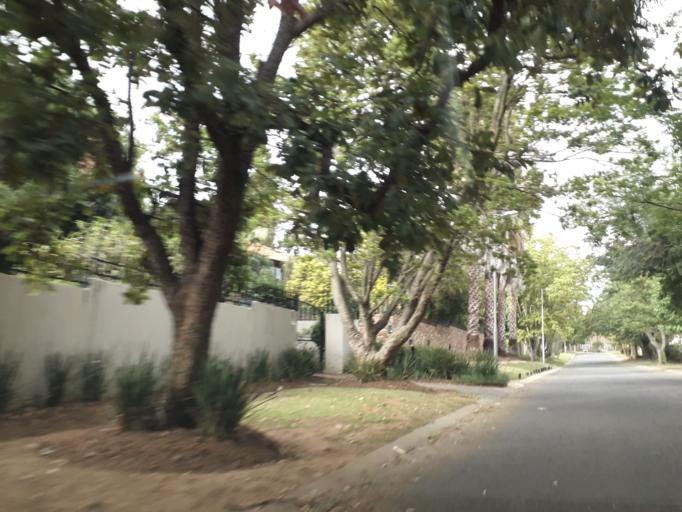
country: ZA
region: Gauteng
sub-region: City of Johannesburg Metropolitan Municipality
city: Roodepoort
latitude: -26.1045
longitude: 27.9583
